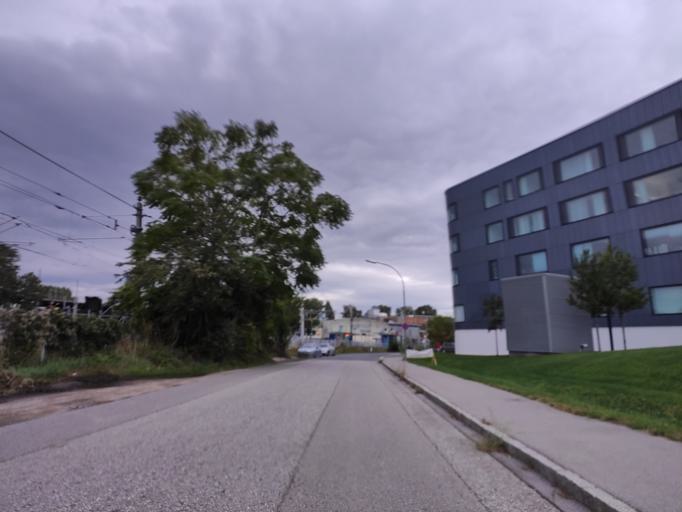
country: AT
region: Lower Austria
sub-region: Politischer Bezirk Baden
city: Pfaffstatten
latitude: 48.0007
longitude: 16.2567
